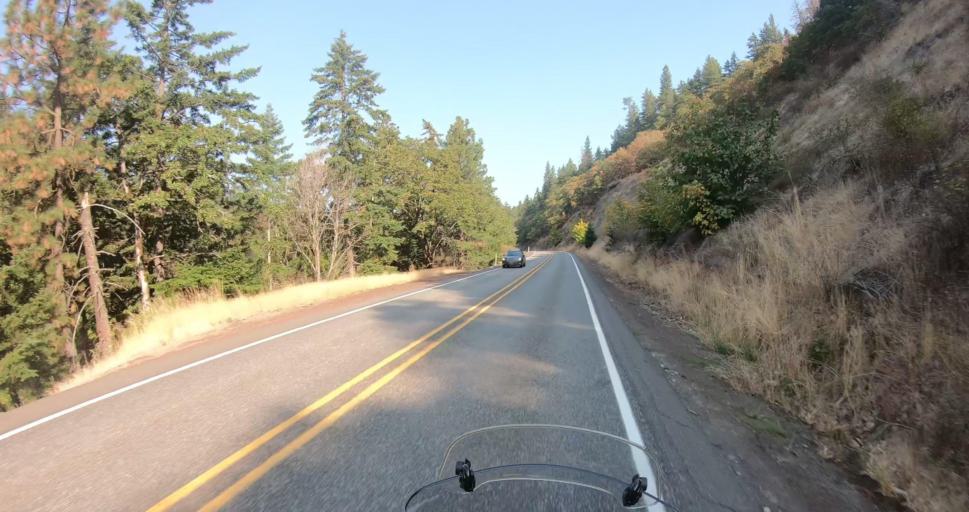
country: US
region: Oregon
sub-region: Hood River County
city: Hood River
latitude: 45.7371
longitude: -121.5218
